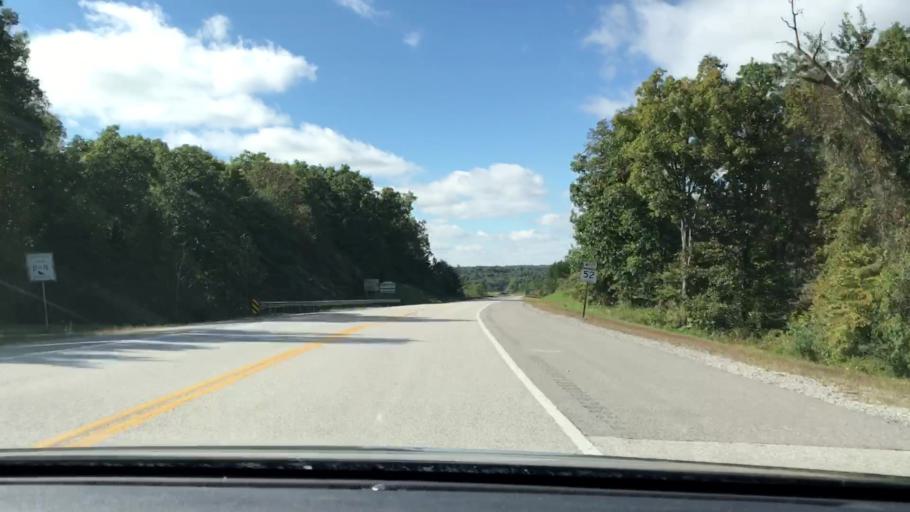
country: US
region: Tennessee
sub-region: Fentress County
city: Jamestown
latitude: 36.3501
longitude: -84.7224
